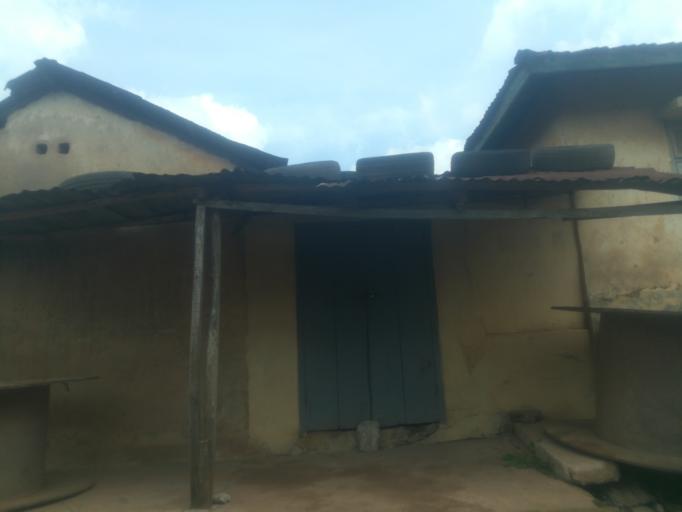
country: NG
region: Oyo
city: Ibadan
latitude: 7.3604
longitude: 3.8816
